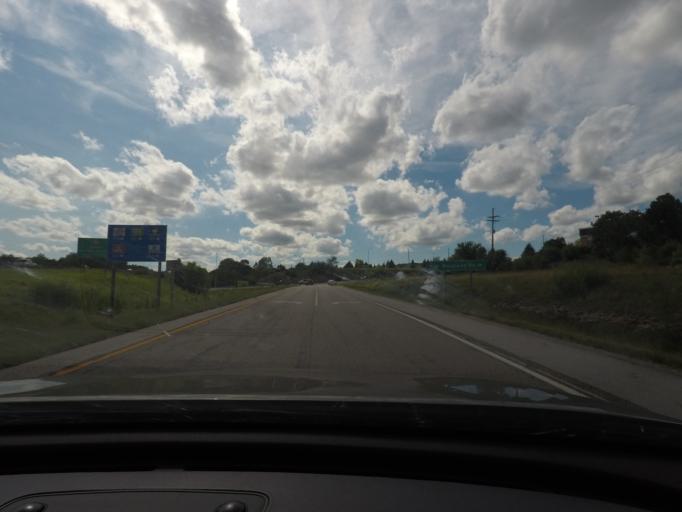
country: US
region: Kansas
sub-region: Johnson County
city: Olathe
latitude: 38.9424
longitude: -94.8147
